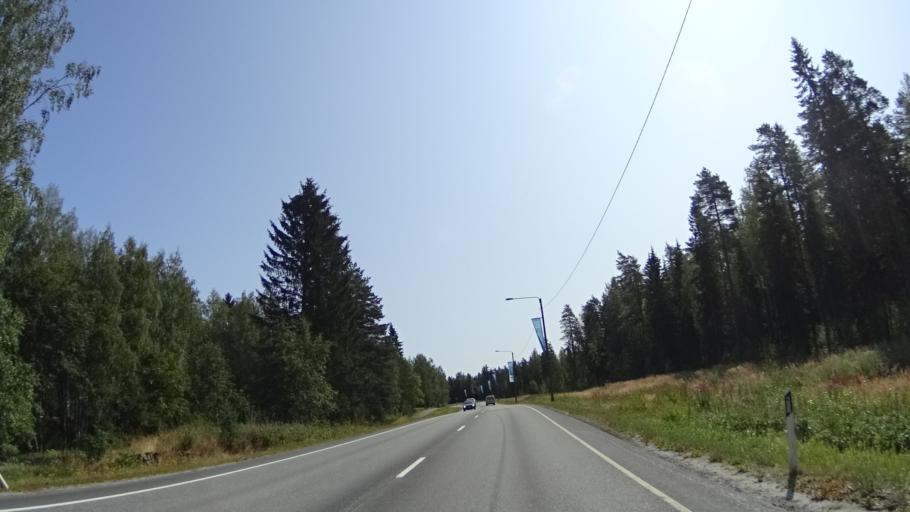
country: FI
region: Pirkanmaa
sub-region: Ylae-Pirkanmaa
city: Maenttae
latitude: 62.0295
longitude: 24.5858
